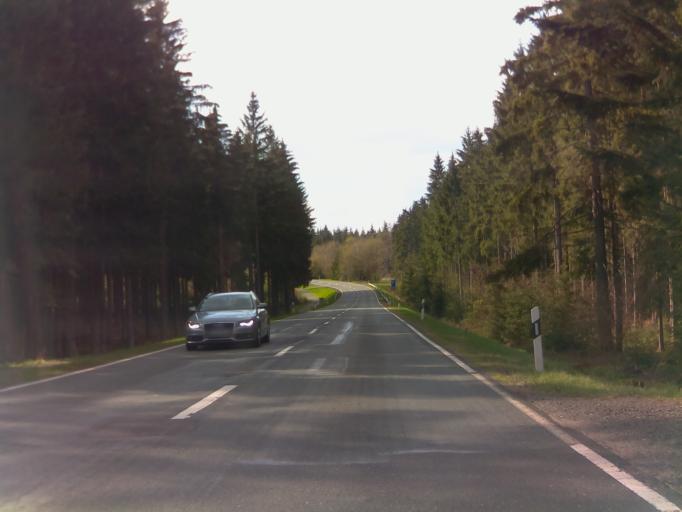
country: DE
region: Bavaria
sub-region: Upper Franconia
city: Ludwigsstadt
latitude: 50.4642
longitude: 11.3352
